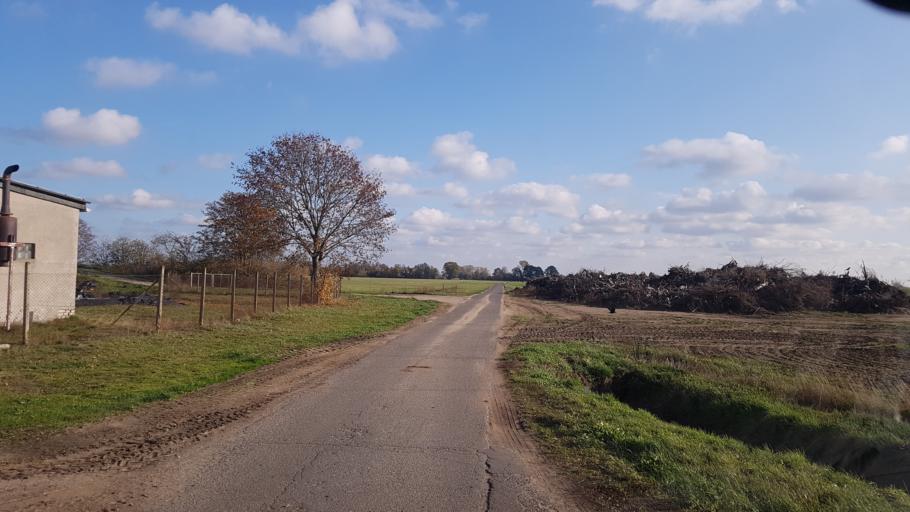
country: DE
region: Brandenburg
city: Doberlug-Kirchhain
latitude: 51.6914
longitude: 13.5185
